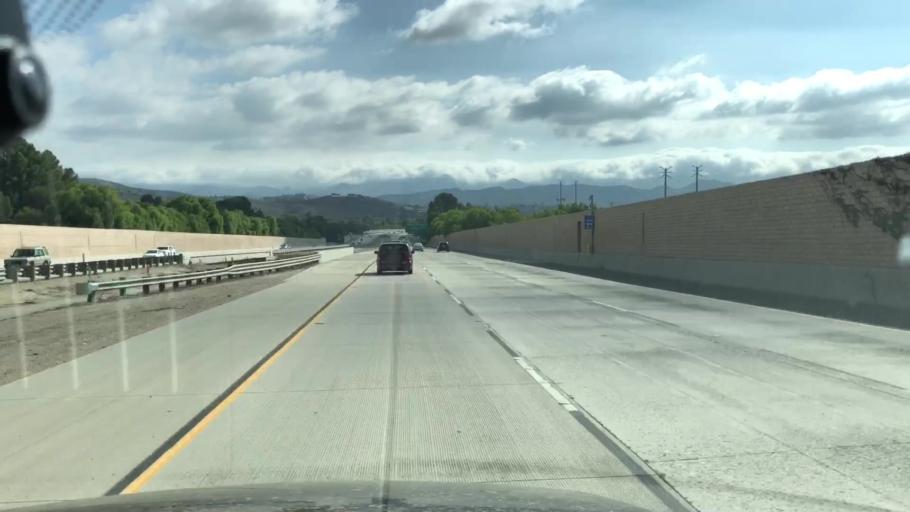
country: US
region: California
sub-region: Ventura County
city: Thousand Oaks
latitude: 34.2189
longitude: -118.8500
